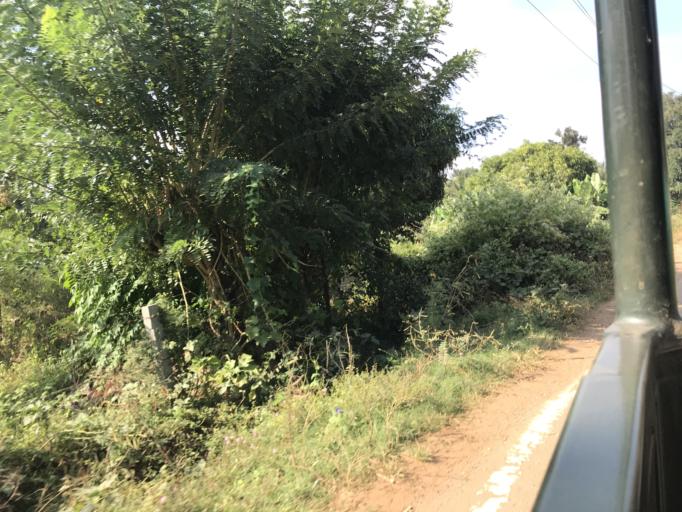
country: IN
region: Karnataka
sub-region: Mysore
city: Heggadadevankote
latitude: 11.9468
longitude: 76.2594
